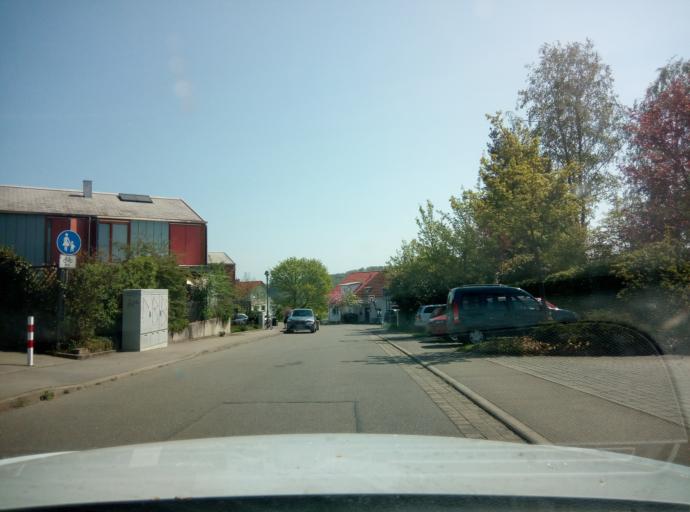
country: DE
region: Baden-Wuerttemberg
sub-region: Tuebingen Region
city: Kusterdingen
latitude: 48.5313
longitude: 9.0918
